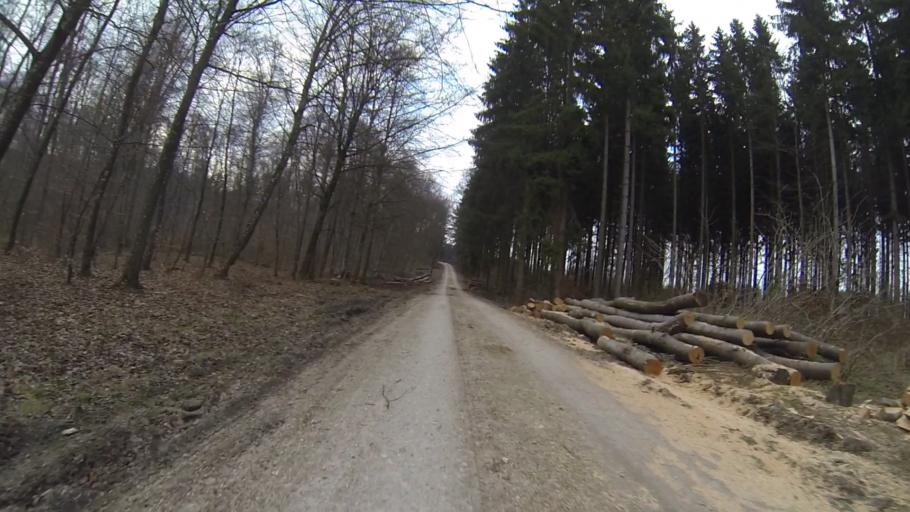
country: DE
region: Baden-Wuerttemberg
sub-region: Regierungsbezirk Stuttgart
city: Bolheim
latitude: 48.6266
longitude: 10.1252
